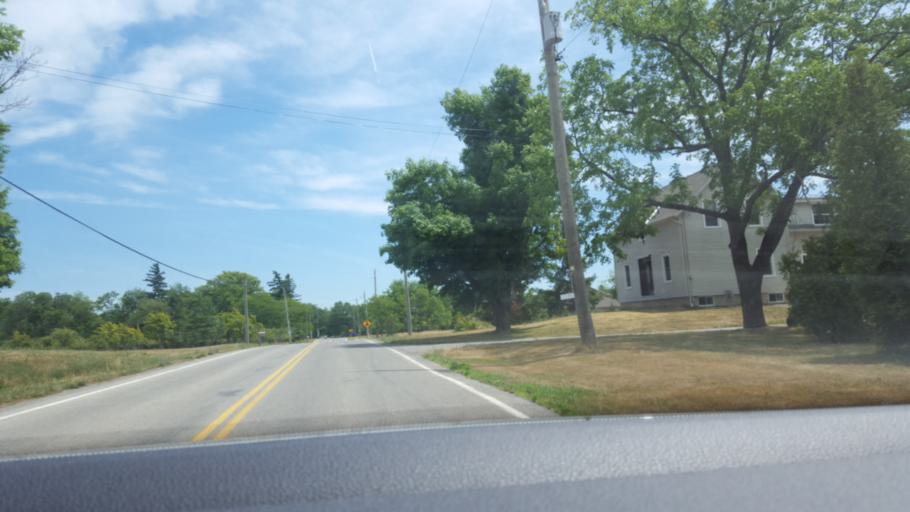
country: CA
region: Ontario
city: Oakville
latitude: 43.1831
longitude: -79.5644
